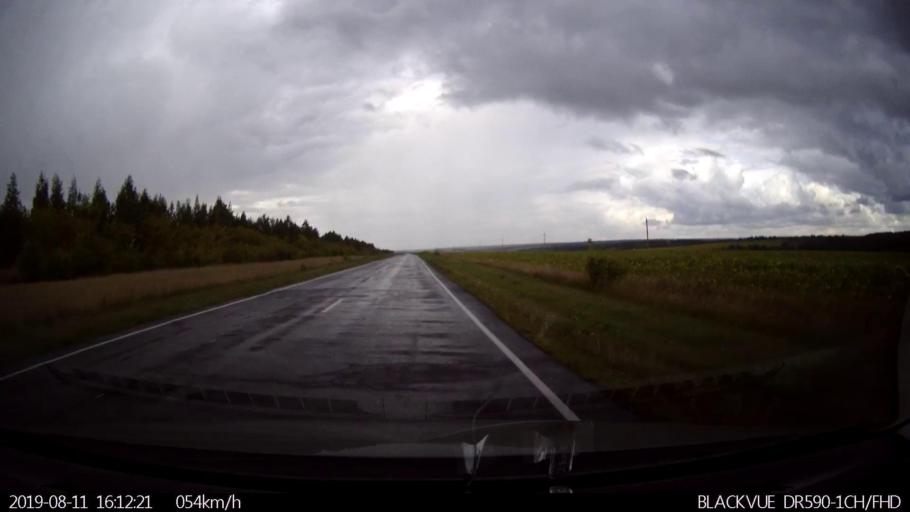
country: RU
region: Ulyanovsk
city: Ignatovka
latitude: 54.0108
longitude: 47.6407
